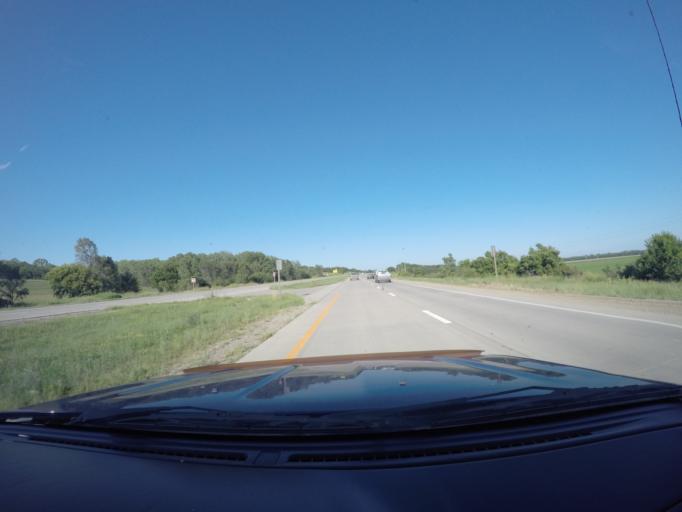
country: US
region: Kansas
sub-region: Shawnee County
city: Topeka
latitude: 39.0875
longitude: -95.5251
